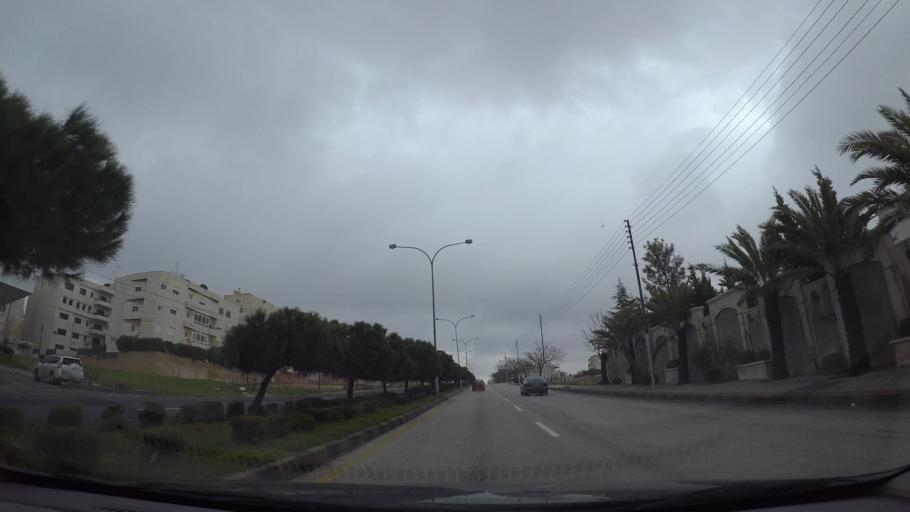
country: JO
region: Amman
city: Wadi as Sir
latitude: 31.9468
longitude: 35.8728
